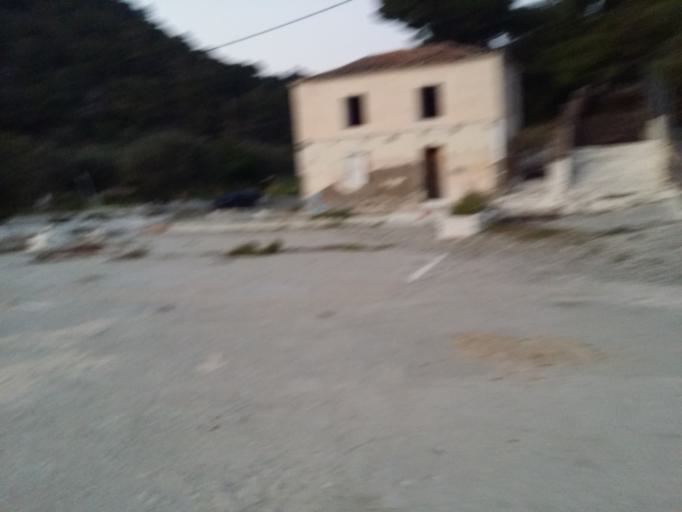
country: GR
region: Attica
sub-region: Nomos Piraios
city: Poros
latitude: 37.5045
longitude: 23.4836
